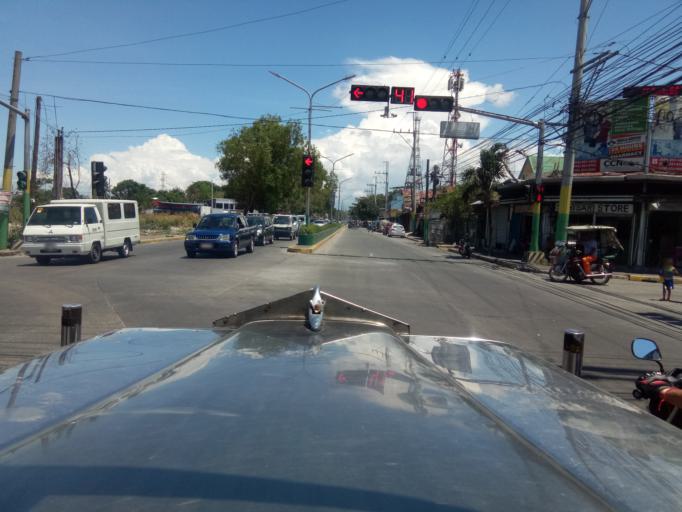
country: PH
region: Calabarzon
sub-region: Province of Cavite
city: Dasmarinas
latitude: 14.3176
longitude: 120.9644
